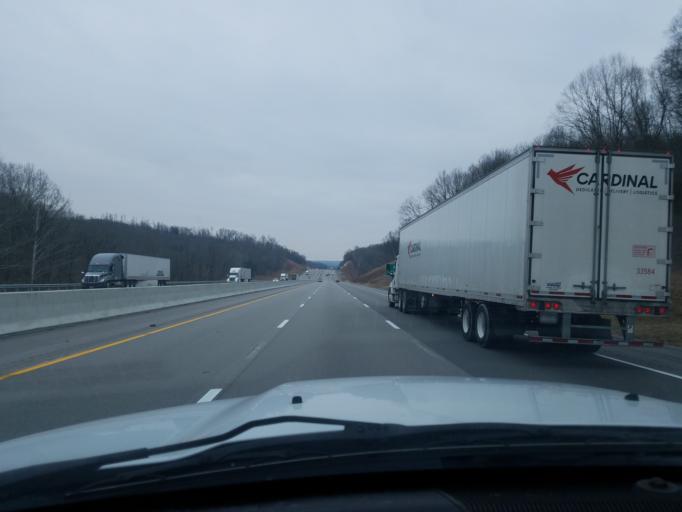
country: US
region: Kentucky
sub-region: Hart County
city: Munfordville
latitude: 37.3147
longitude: -85.9048
